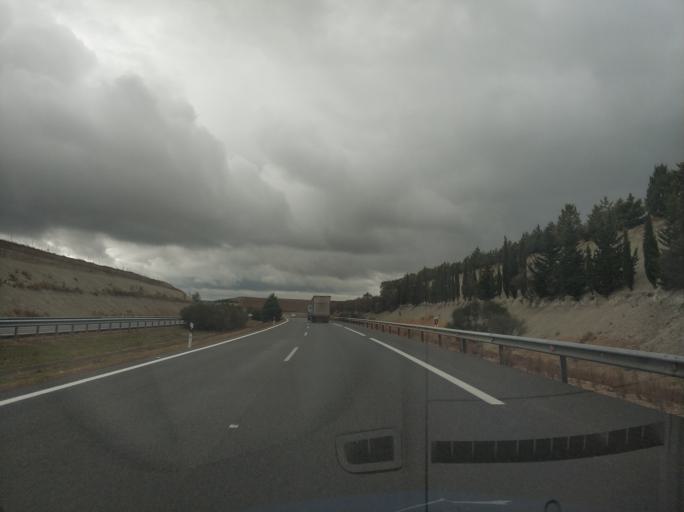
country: ES
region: Castille and Leon
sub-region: Provincia de Palencia
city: Soto de Cerrato
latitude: 41.9682
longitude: -4.4559
